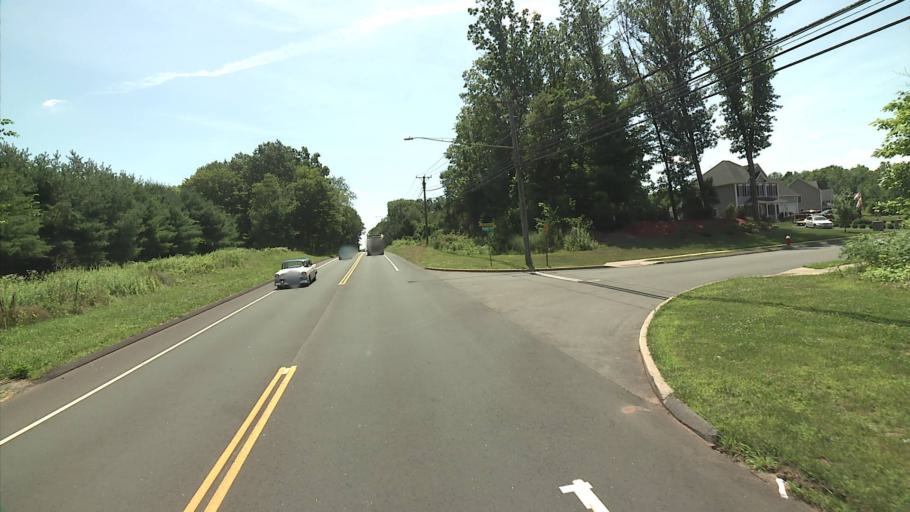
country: US
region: Connecticut
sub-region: Hartford County
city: Kensington
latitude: 41.6138
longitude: -72.7252
